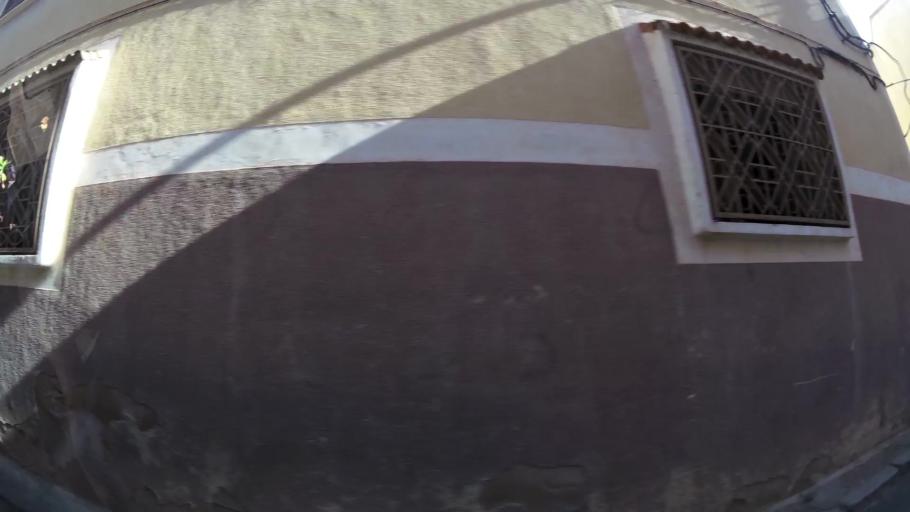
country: MA
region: Oriental
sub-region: Oujda-Angad
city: Oujda
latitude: 34.6758
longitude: -1.9085
